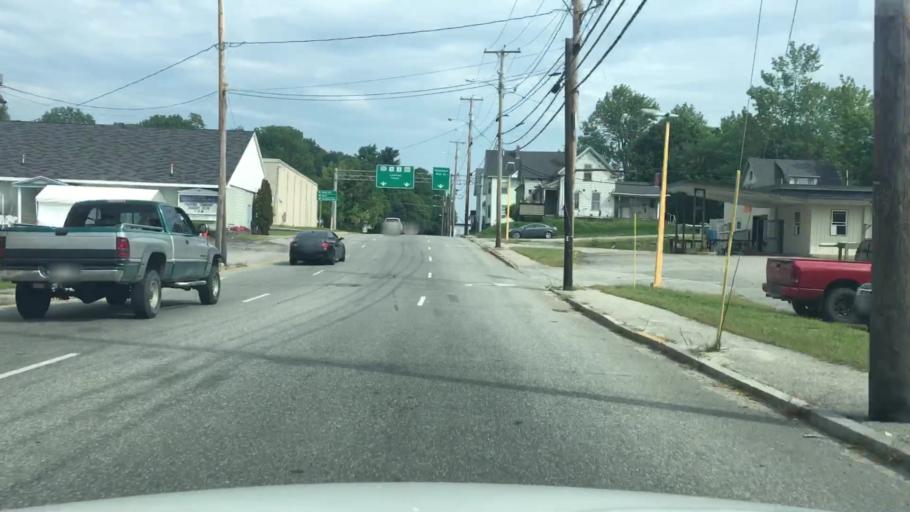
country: US
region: Maine
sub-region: Androscoggin County
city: Auburn
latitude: 44.0880
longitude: -70.2313
